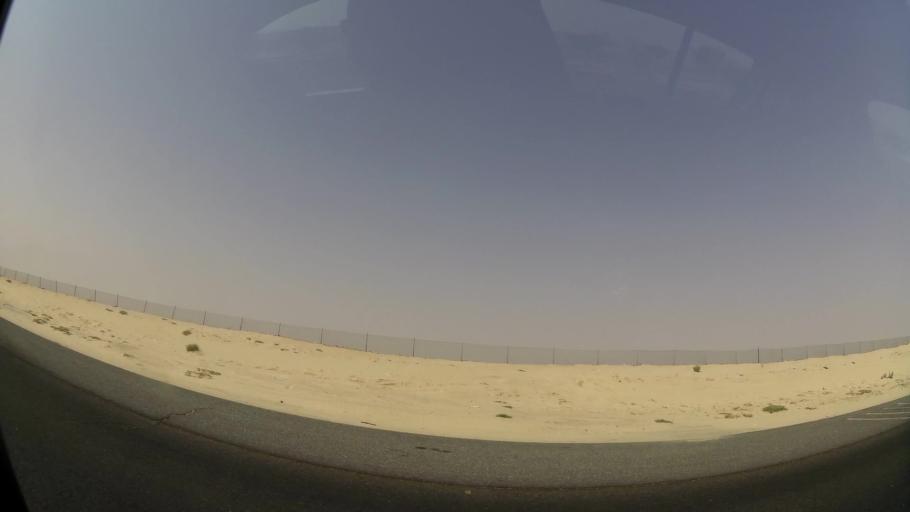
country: KW
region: Muhafazat al Jahra'
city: Al Jahra'
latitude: 29.3552
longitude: 47.6334
